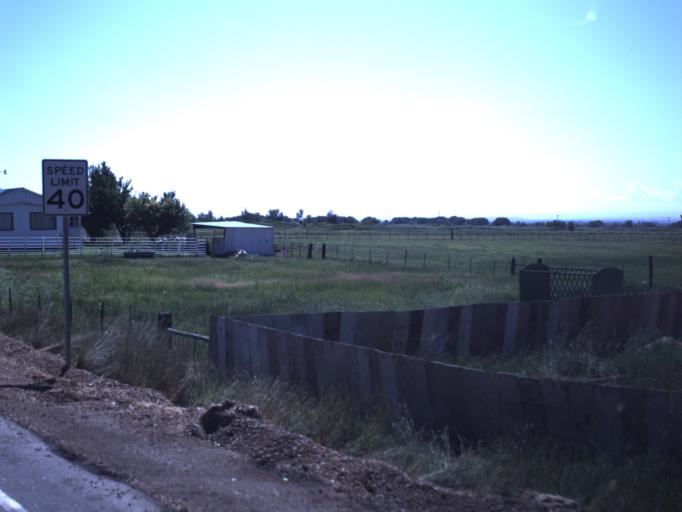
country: US
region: Utah
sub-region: Duchesne County
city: Roosevelt
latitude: 40.4330
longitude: -110.0250
